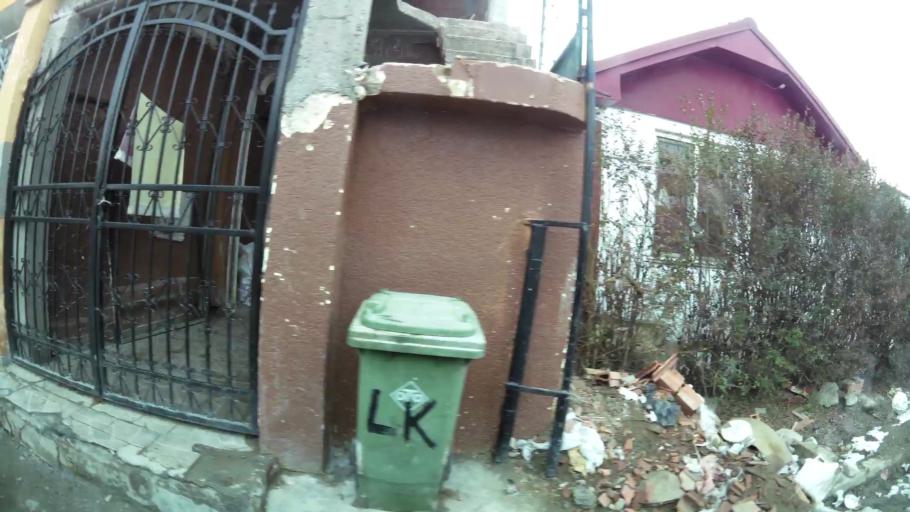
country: MK
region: Suto Orizari
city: Suto Orizare
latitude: 42.0359
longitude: 21.4229
